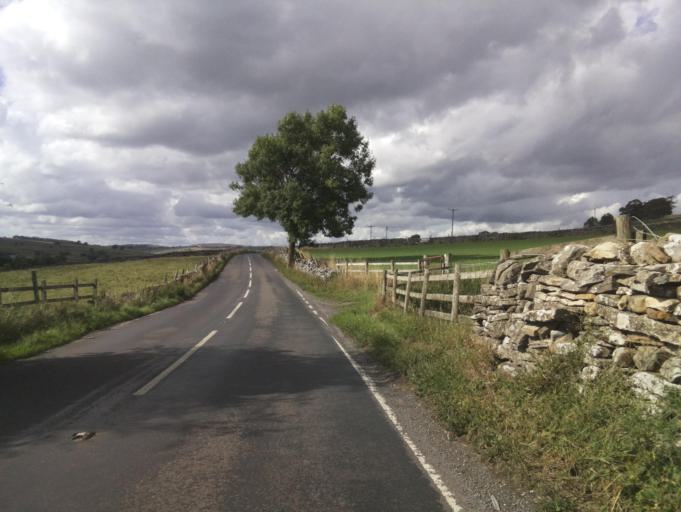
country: GB
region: England
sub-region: North Yorkshire
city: Leyburn
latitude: 54.3628
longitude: -1.8199
